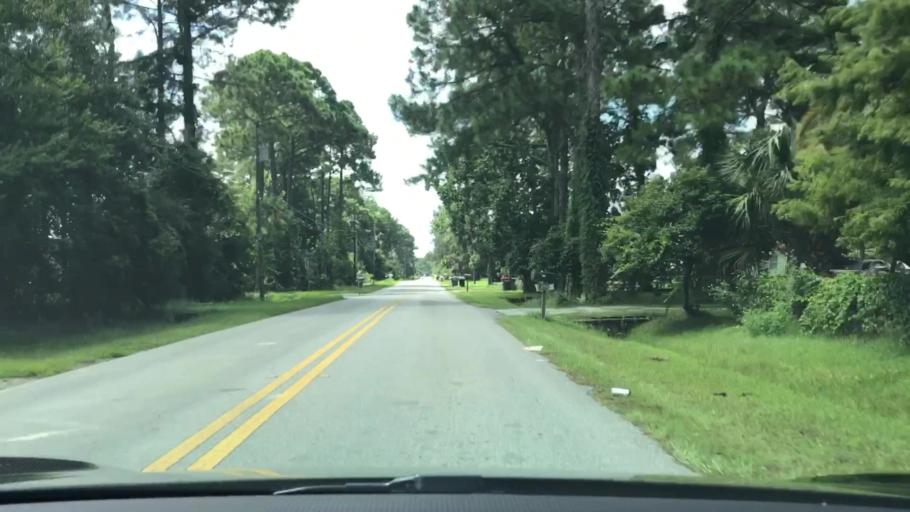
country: US
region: Florida
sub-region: Bay County
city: Panama City Beach
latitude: 30.1773
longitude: -85.7866
